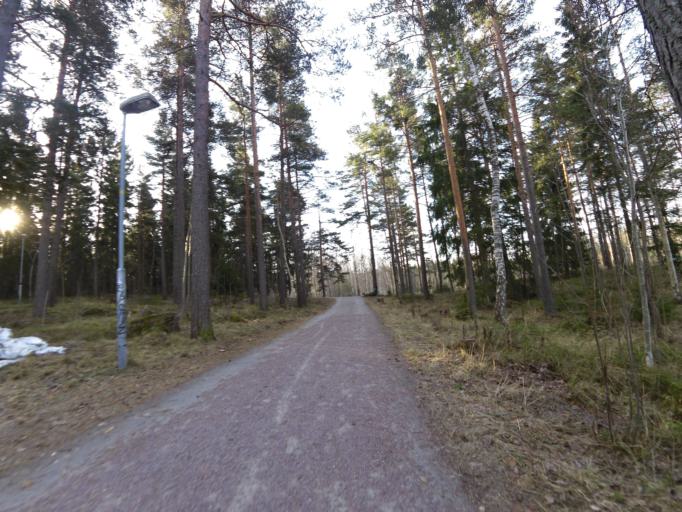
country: SE
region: Gaevleborg
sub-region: Gavle Kommun
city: Gavle
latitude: 60.6573
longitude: 17.1405
